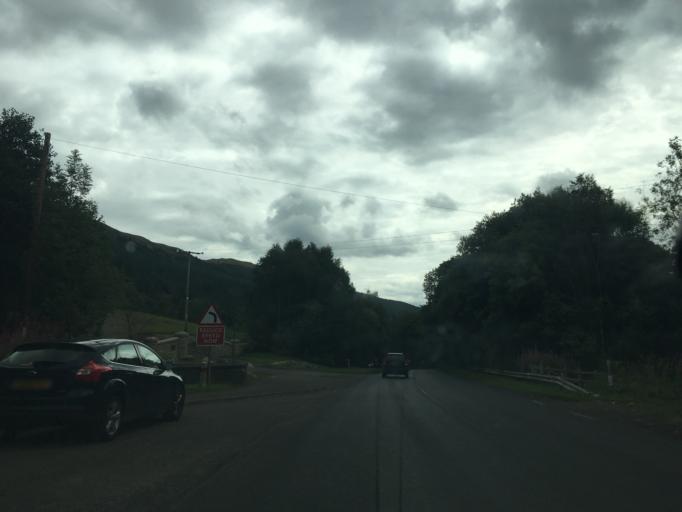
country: GB
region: Scotland
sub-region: Stirling
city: Callander
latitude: 56.2947
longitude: -4.2914
